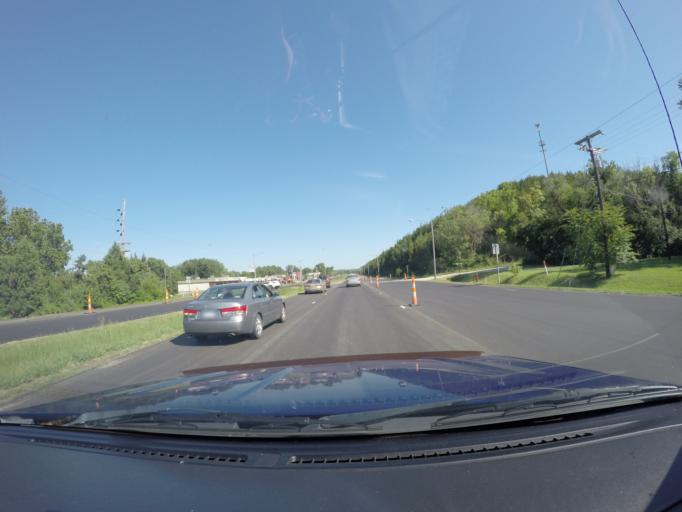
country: US
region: Kansas
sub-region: Riley County
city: Manhattan
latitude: 39.2066
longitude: -96.5701
